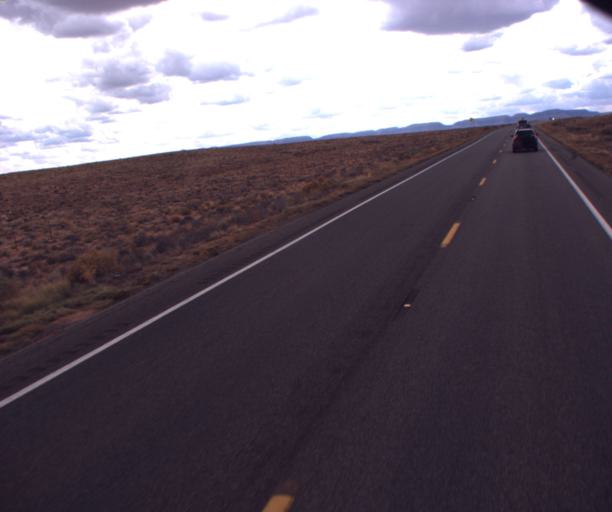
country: US
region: Arizona
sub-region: Navajo County
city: Kayenta
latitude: 36.7431
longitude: -110.0759
